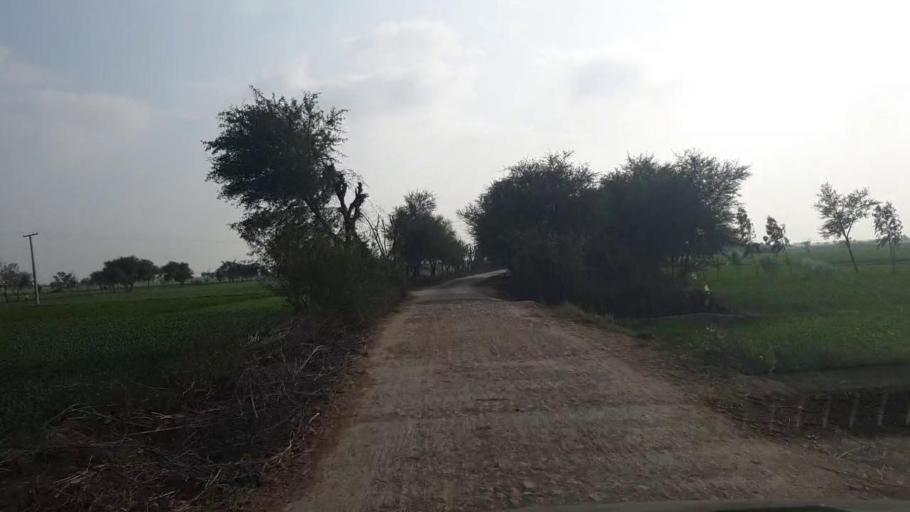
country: PK
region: Sindh
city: Shahdadpur
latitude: 25.8803
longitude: 68.6664
